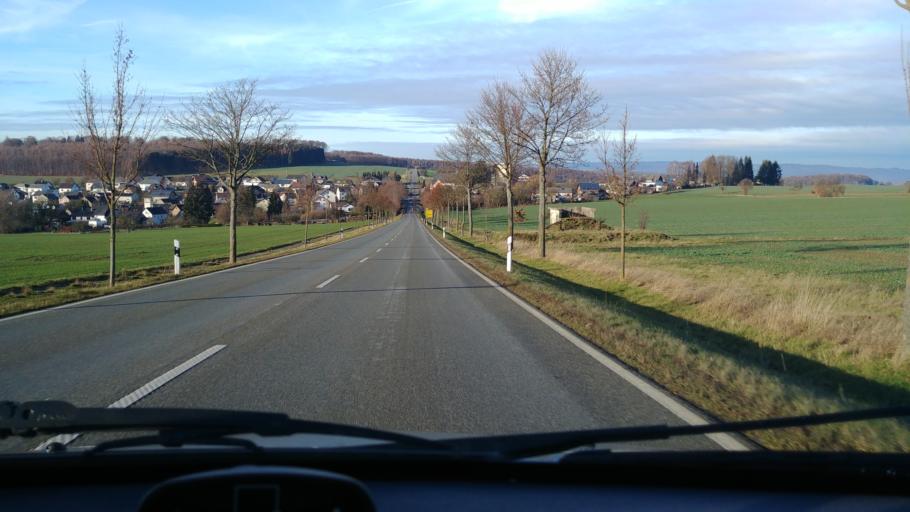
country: DE
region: Rheinland-Pfalz
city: Pohl
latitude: 50.2463
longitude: 7.8713
